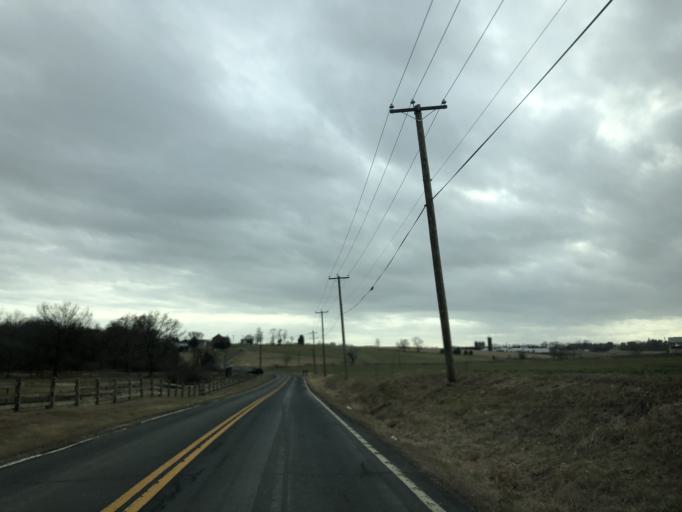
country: US
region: Maryland
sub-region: Cecil County
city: North East
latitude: 39.6841
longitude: -75.9508
